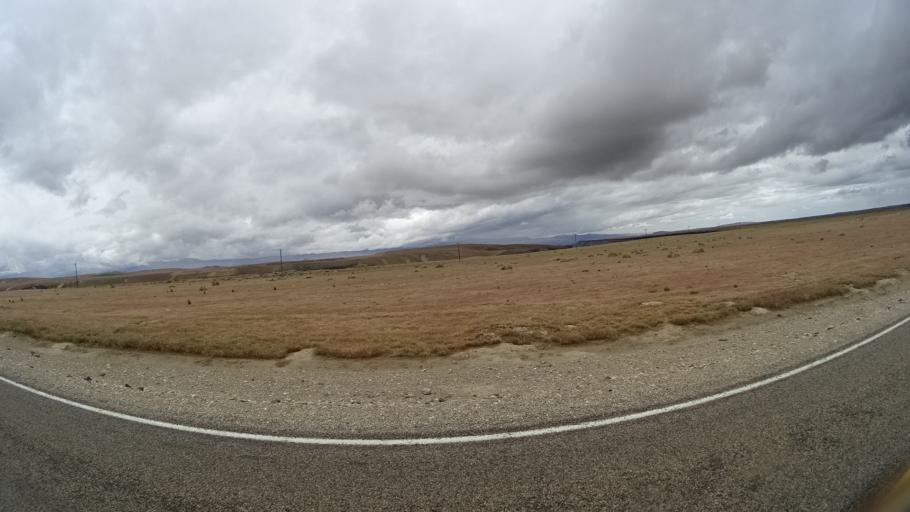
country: US
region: Idaho
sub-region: Owyhee County
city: Murphy
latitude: 43.2799
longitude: -116.3942
